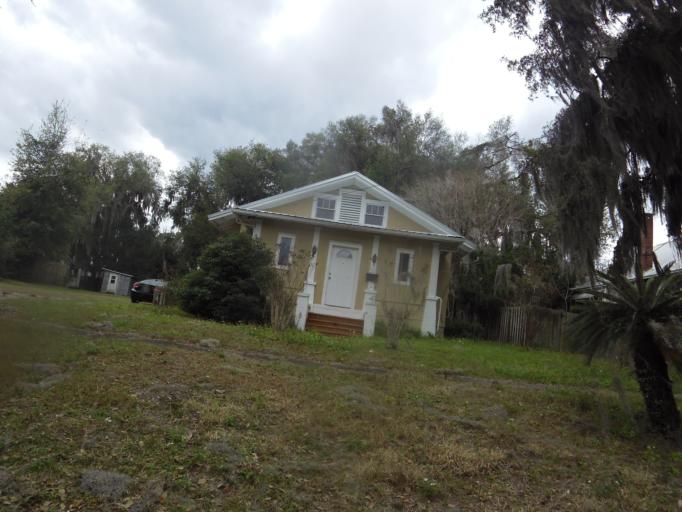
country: US
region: Florida
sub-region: Putnam County
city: Crescent City
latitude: 29.4309
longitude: -81.5082
